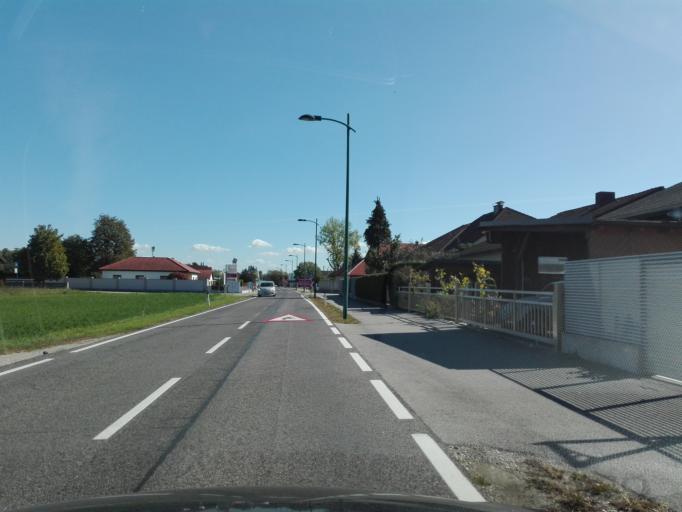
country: AT
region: Lower Austria
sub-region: Politischer Bezirk Amstetten
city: Ennsdorf
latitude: 48.2060
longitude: 14.5008
